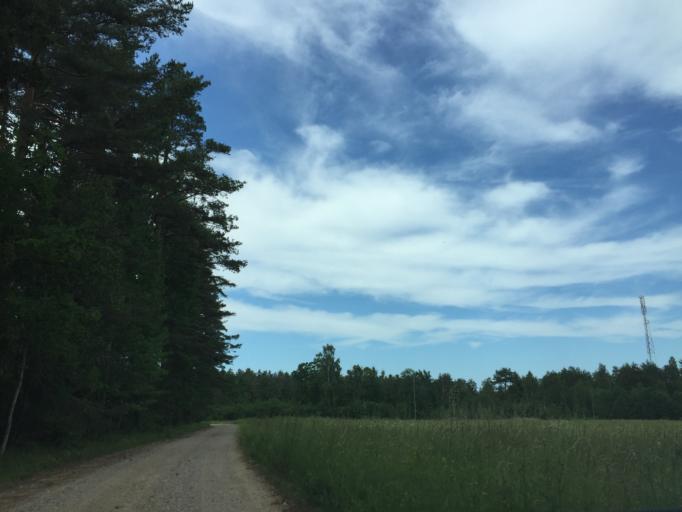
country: LV
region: Engure
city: Smarde
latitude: 57.0504
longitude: 23.2891
